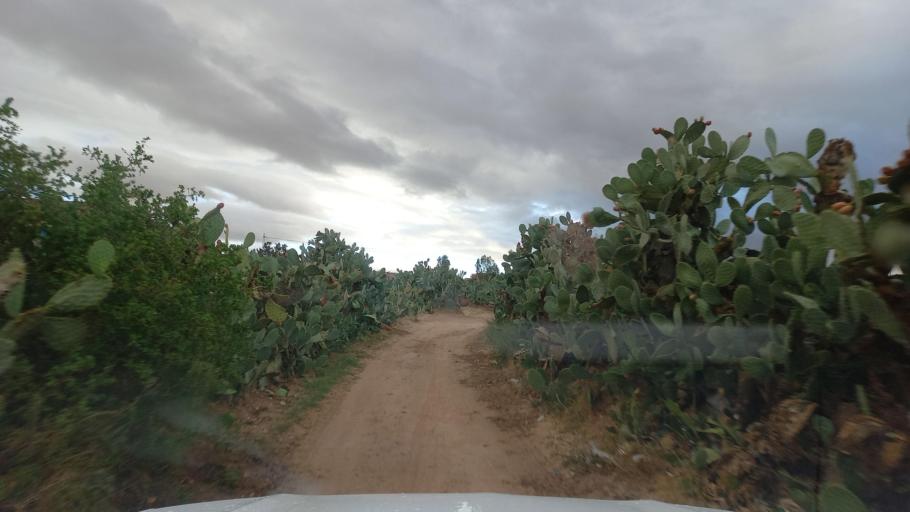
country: TN
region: Al Qasrayn
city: Kasserine
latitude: 35.2599
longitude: 8.9340
